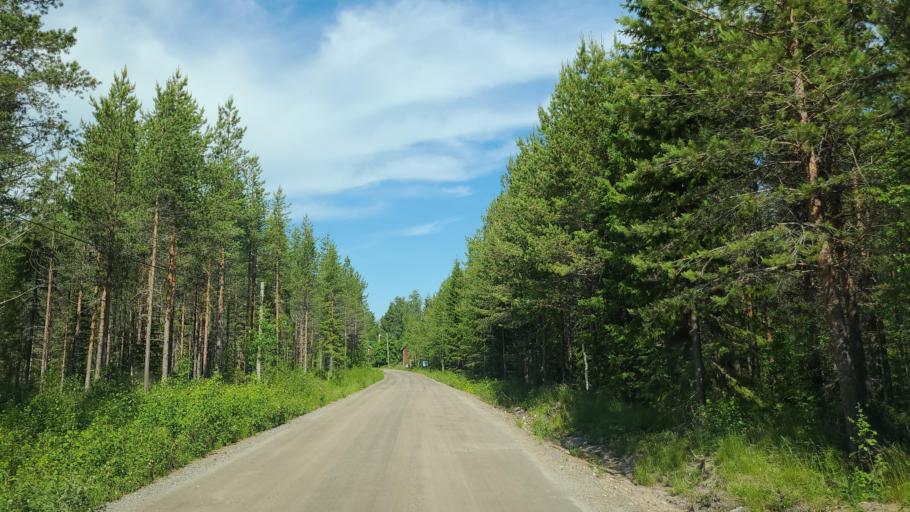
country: SE
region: Vaesterbotten
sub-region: Robertsfors Kommun
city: Robertsfors
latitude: 64.1518
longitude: 20.9508
